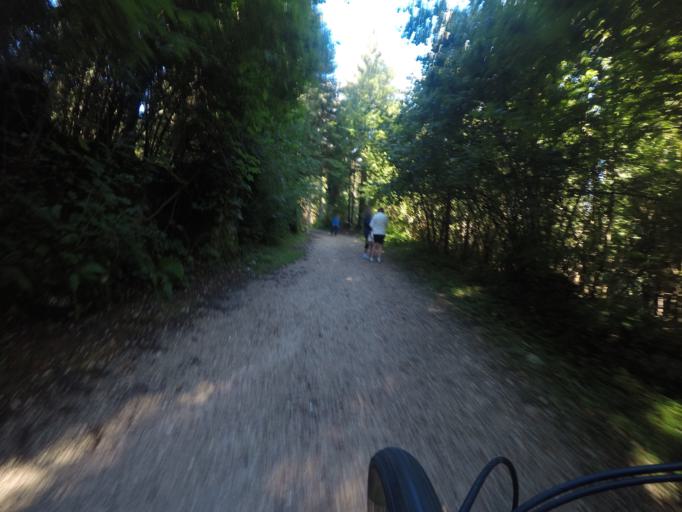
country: IT
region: Veneto
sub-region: Provincia di Vicenza
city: Canove di Roana
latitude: 45.8390
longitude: 11.4457
